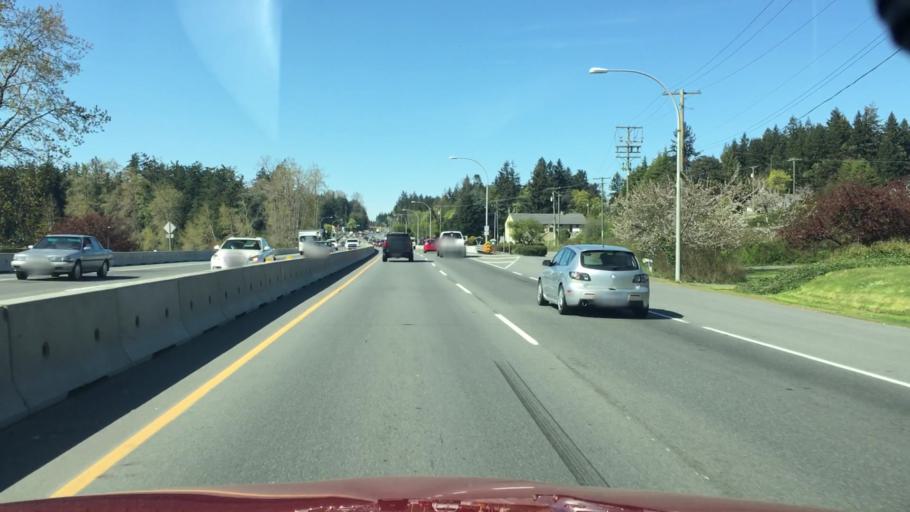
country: CA
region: British Columbia
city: Victoria
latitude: 48.5312
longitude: -123.3879
